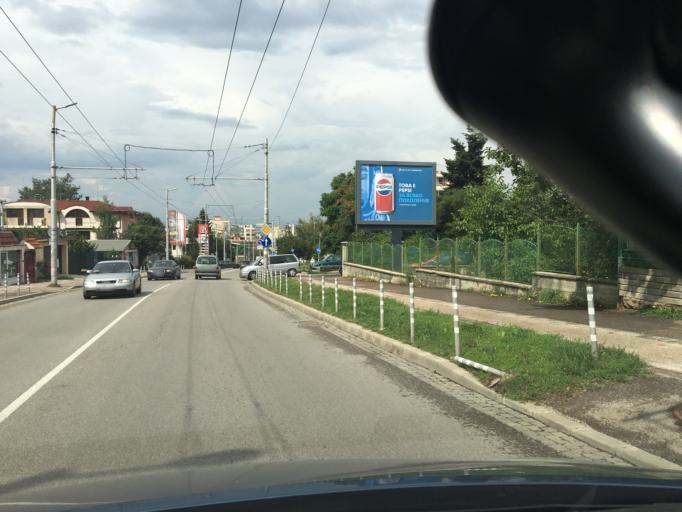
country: BG
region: Sofia-Capital
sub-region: Stolichna Obshtina
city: Sofia
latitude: 42.6596
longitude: 23.2728
